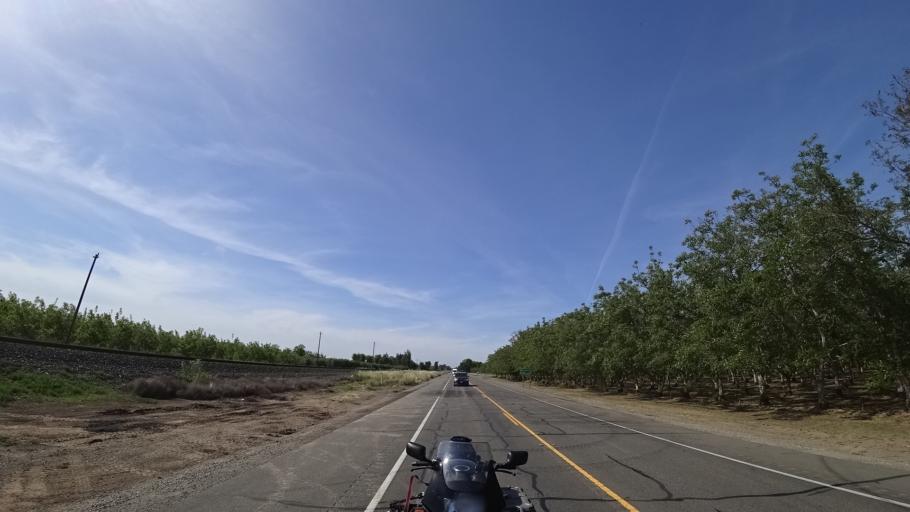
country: US
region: California
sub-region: Tehama County
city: Los Molinos
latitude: 40.0048
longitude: -122.0917
